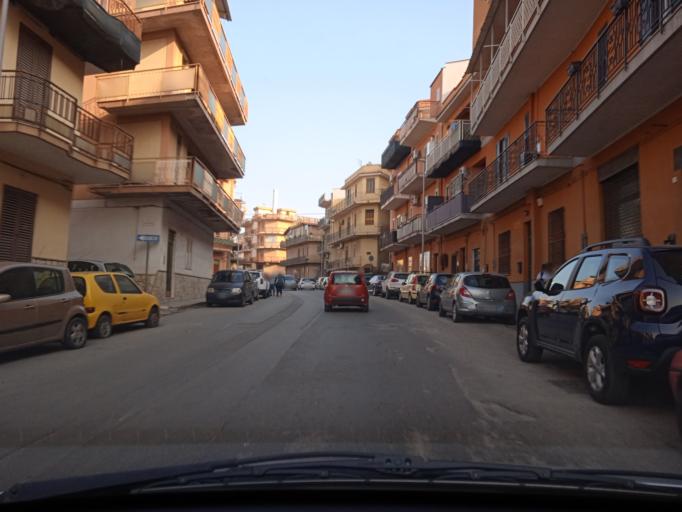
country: IT
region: Sicily
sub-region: Palermo
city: Villabate
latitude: 38.0760
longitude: 13.4403
